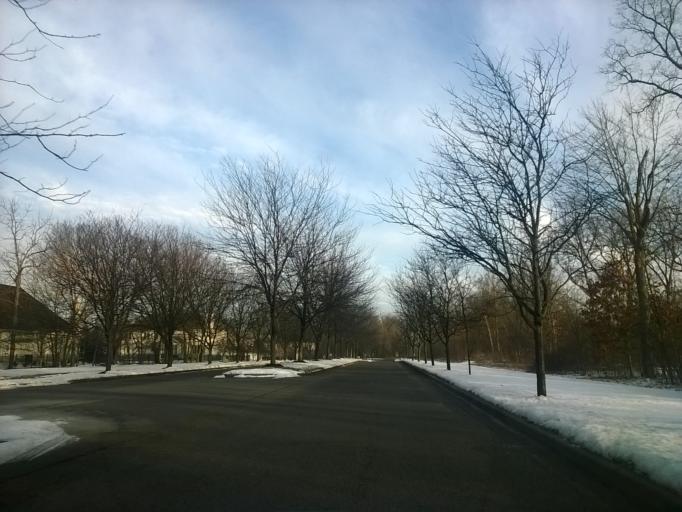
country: US
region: Indiana
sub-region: Hamilton County
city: Fishers
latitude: 39.9831
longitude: -86.0482
